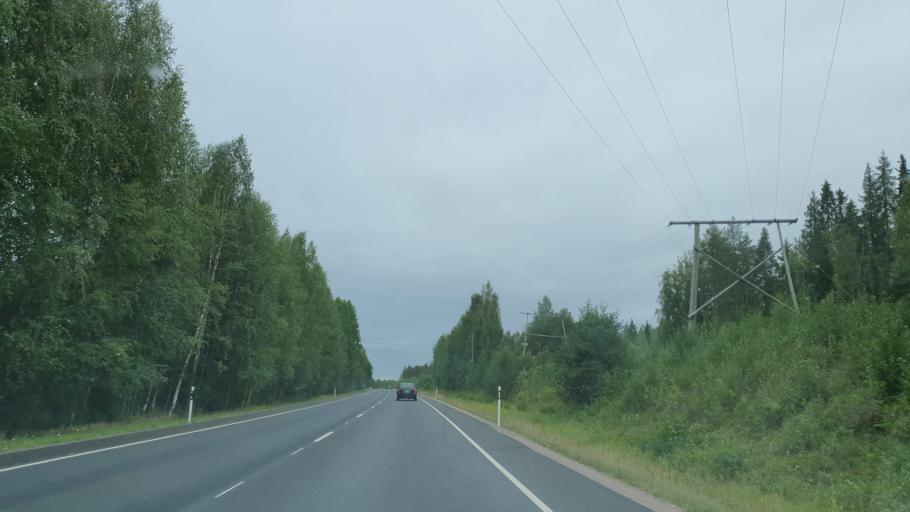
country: FI
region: Lapland
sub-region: Rovaniemi
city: Rovaniemi
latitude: 66.6055
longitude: 25.5772
